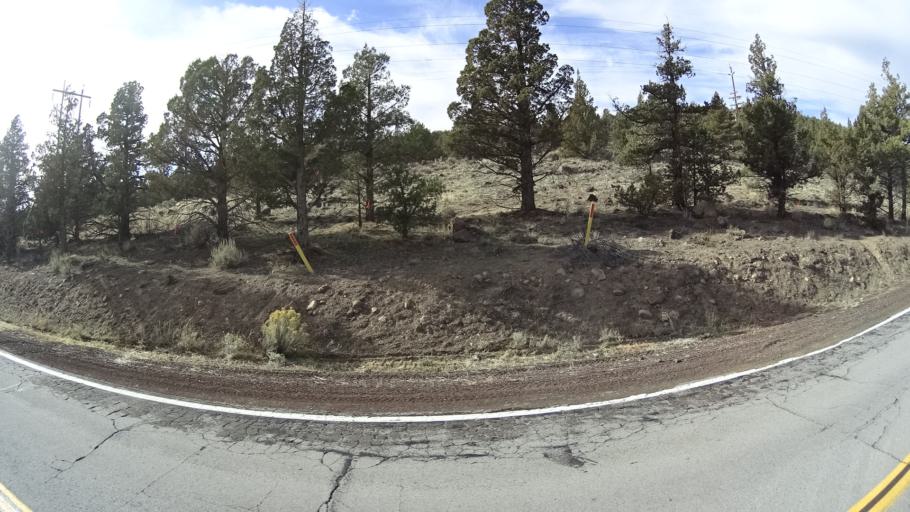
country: US
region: California
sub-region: Siskiyou County
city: Weed
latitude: 41.5370
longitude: -122.3646
